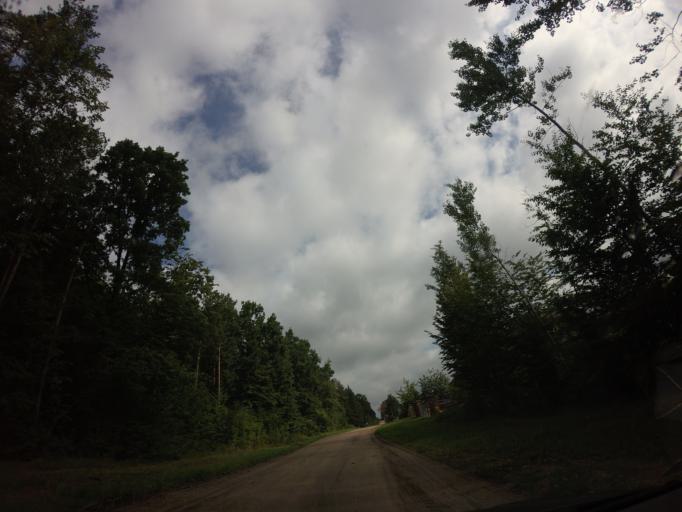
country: PL
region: Podlasie
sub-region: Bialystok
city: Bialystok
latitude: 53.0919
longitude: 23.2028
